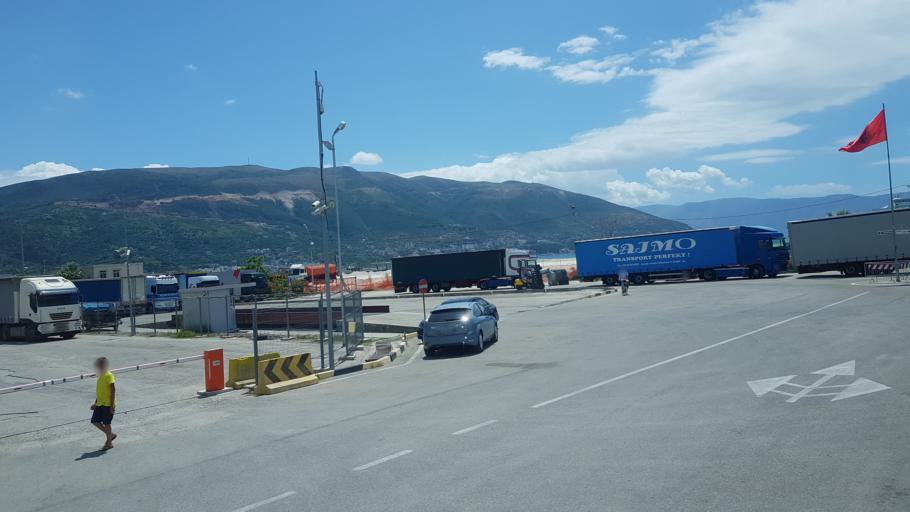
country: AL
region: Vlore
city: Vlore
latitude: 40.4528
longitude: 19.4830
